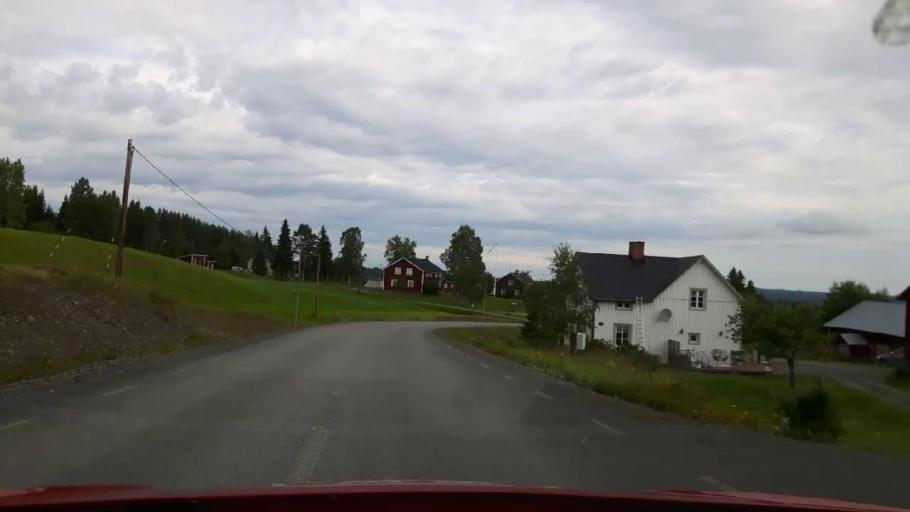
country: SE
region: Jaemtland
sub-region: OEstersunds Kommun
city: Lit
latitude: 63.4232
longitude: 15.2584
